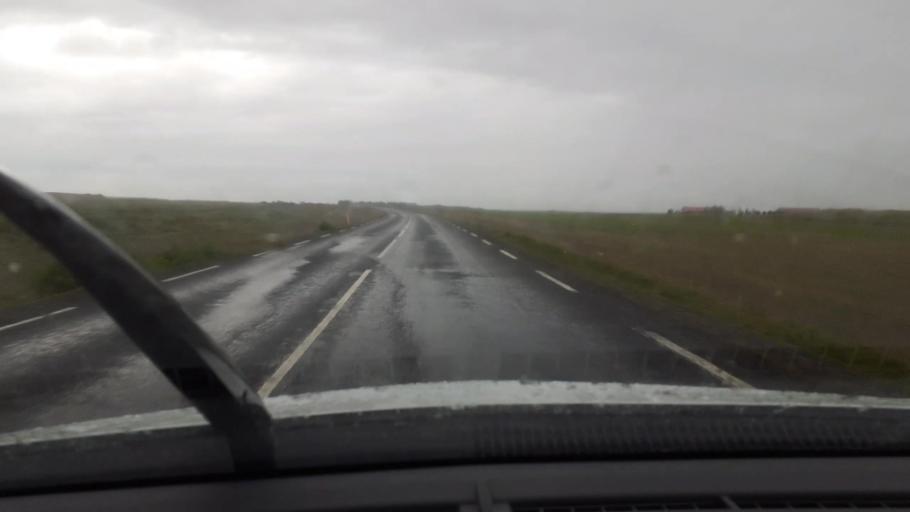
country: IS
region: West
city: Akranes
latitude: 64.3657
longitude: -21.9211
